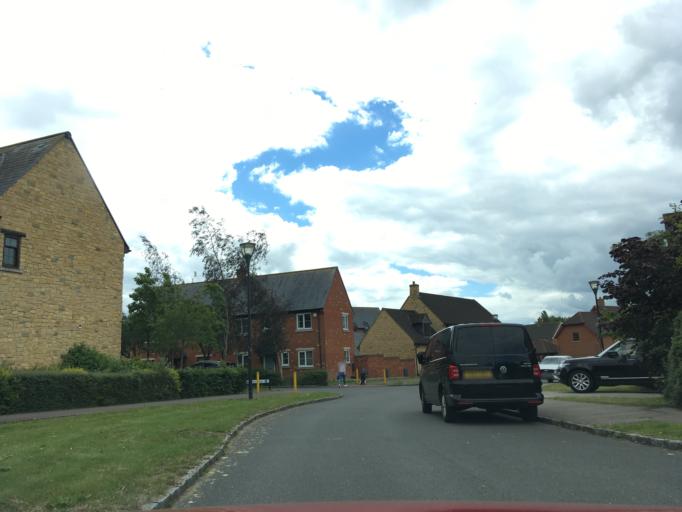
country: GB
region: England
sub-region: Milton Keynes
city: Simpson
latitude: 52.0335
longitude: -0.7117
